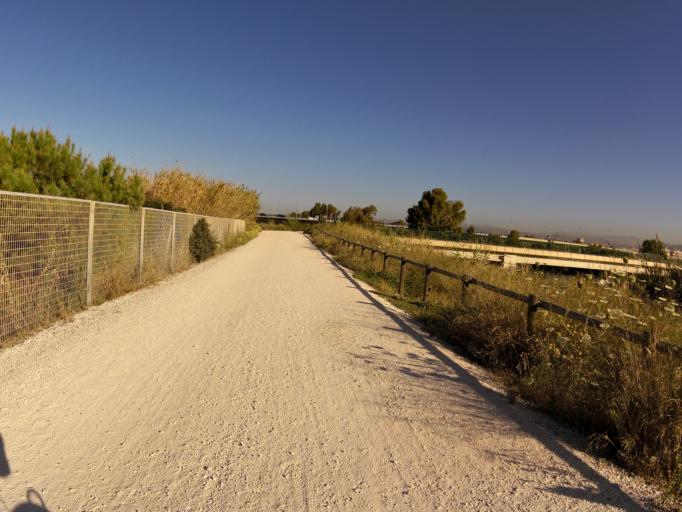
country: ES
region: Andalusia
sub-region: Provincia de Malaga
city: Torremolinos
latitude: 36.6722
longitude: -4.4633
